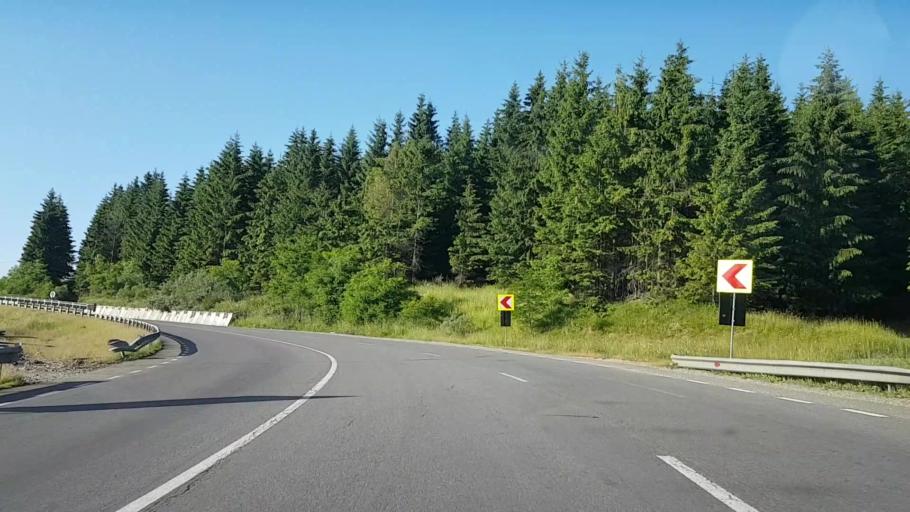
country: RO
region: Bistrita-Nasaud
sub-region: Comuna Lunca Ilvei
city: Lunca Ilvei
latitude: 47.2407
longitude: 25.0190
